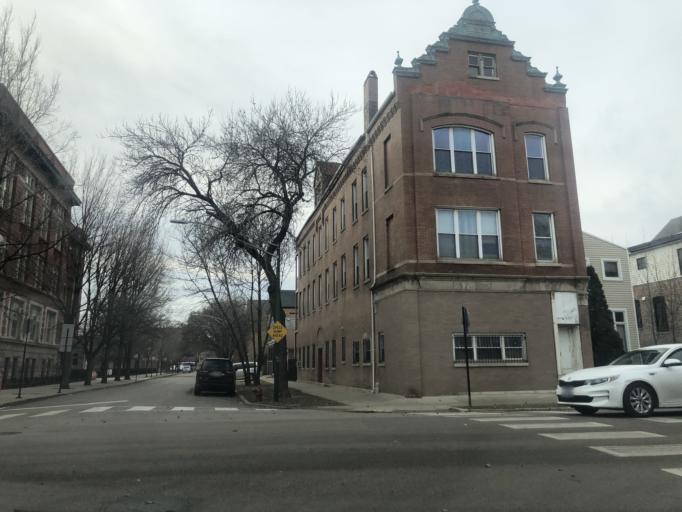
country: US
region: Illinois
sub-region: Cook County
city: Chicago
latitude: 41.9128
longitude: -87.6690
